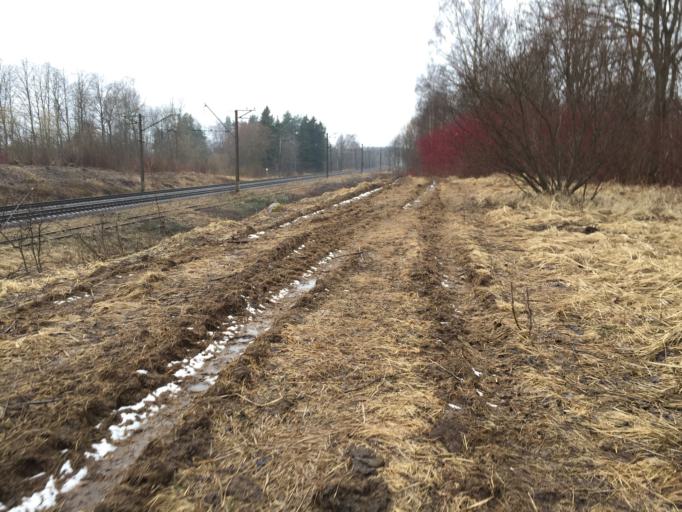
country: LV
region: Lielvarde
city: Lielvarde
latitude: 56.7251
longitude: 24.7866
